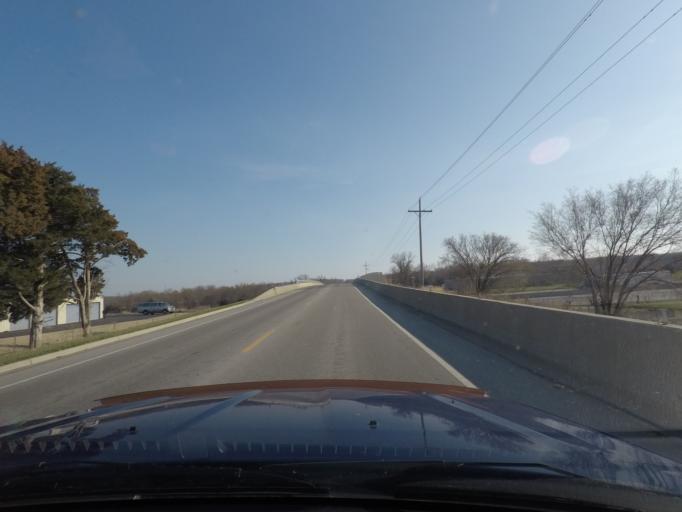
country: US
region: Kansas
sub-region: Douglas County
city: Lawrence
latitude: 38.9910
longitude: -95.2605
